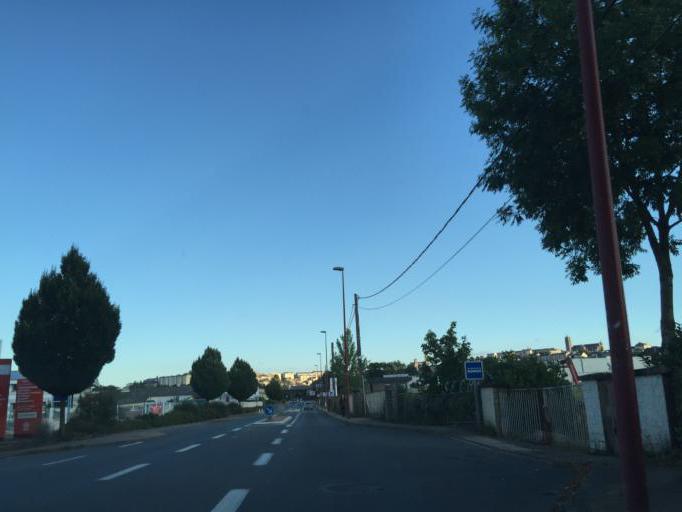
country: FR
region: Midi-Pyrenees
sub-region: Departement de l'Aveyron
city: Rodez
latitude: 44.3687
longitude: 2.5705
